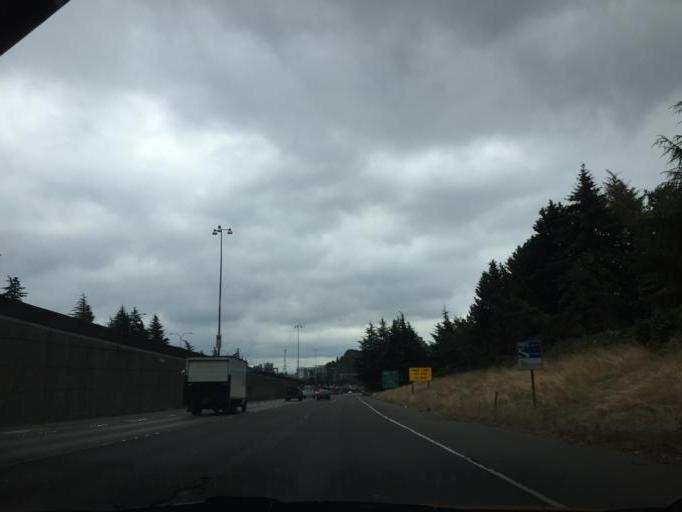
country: US
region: Washington
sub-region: King County
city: Seattle
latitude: 47.6017
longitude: -122.3253
